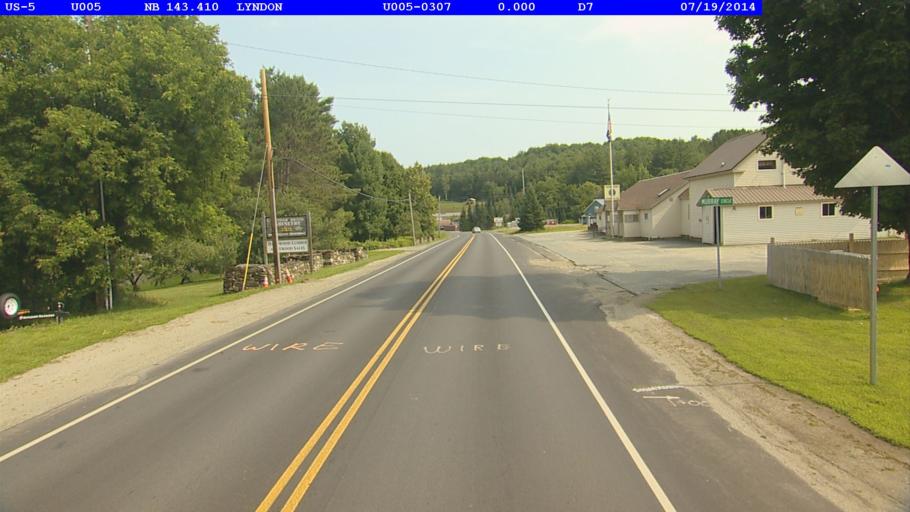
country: US
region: Vermont
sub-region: Caledonia County
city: Lyndon
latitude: 44.4986
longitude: -72.0043
